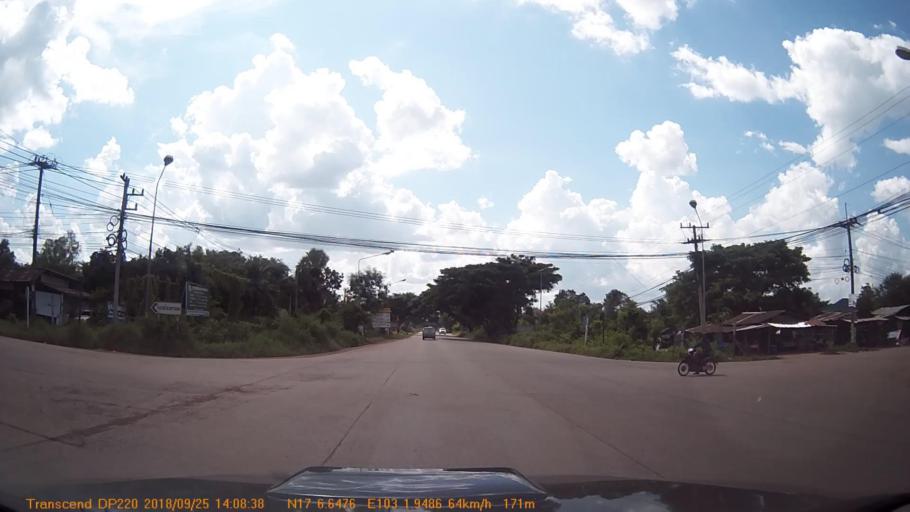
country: TH
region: Changwat Udon Thani
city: Kumphawapi
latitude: 17.1108
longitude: 103.0323
